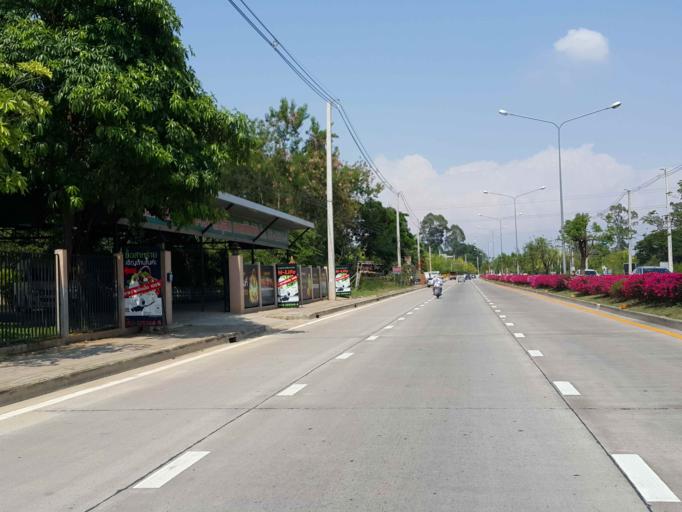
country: TH
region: Chiang Mai
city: Saraphi
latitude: 18.7434
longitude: 99.0087
